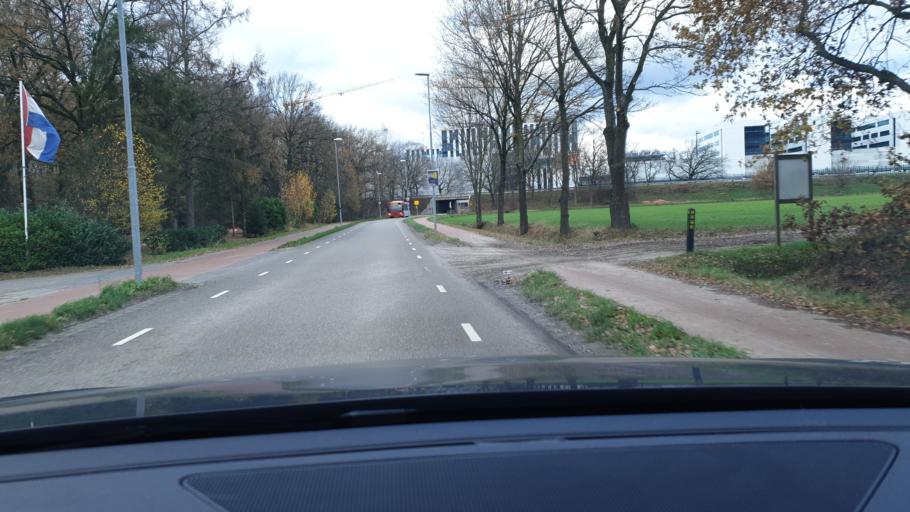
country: NL
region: North Brabant
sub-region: Gemeente Veldhoven
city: Veldhoven
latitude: 51.3991
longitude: 5.4124
